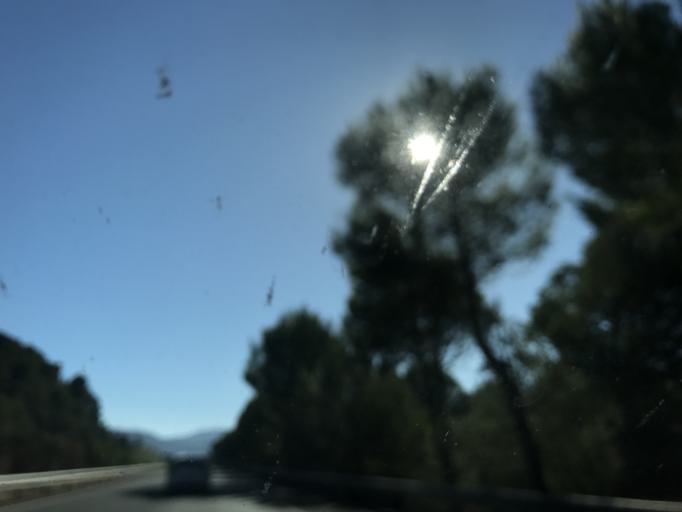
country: ES
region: Andalusia
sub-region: Provincia de Malaga
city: Antequera
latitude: 37.0288
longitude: -4.4886
